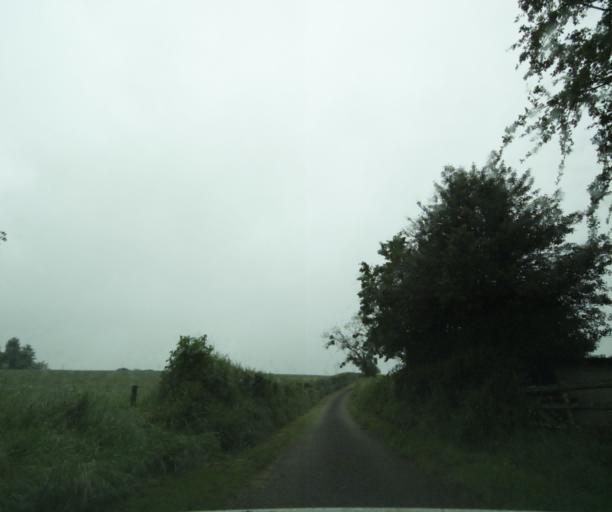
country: FR
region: Bourgogne
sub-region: Departement de Saone-et-Loire
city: Charolles
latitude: 46.4170
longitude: 4.3760
